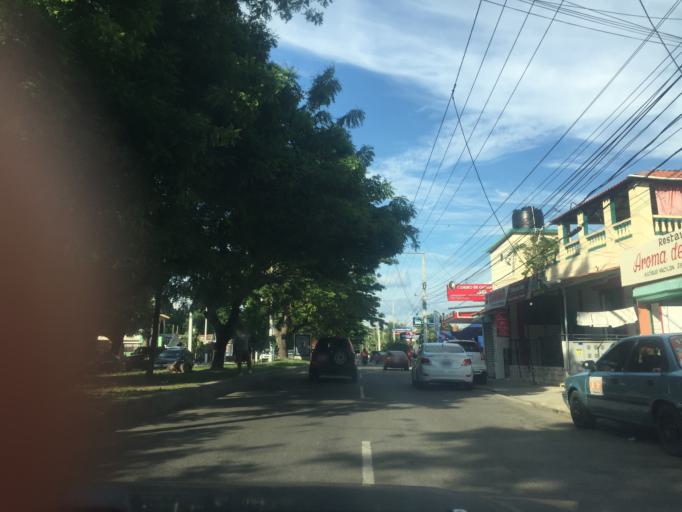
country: DO
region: Santiago
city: Santiago de los Caballeros
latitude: 19.4413
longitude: -70.7147
